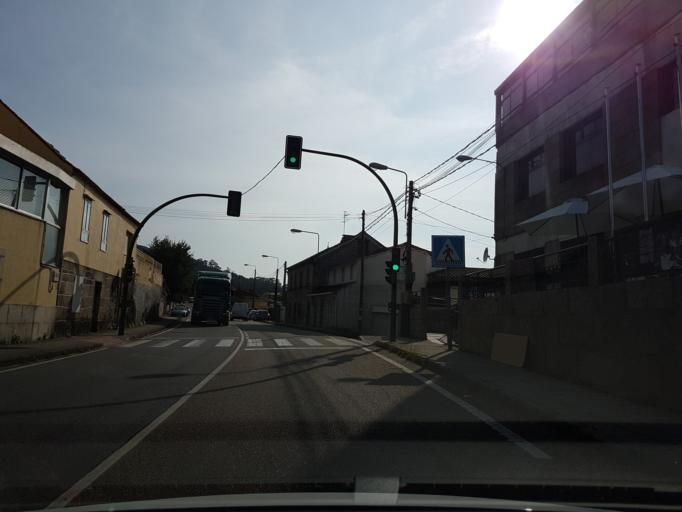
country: ES
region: Galicia
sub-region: Provincia de Pontevedra
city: Nigran
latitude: 42.1926
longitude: -8.7742
